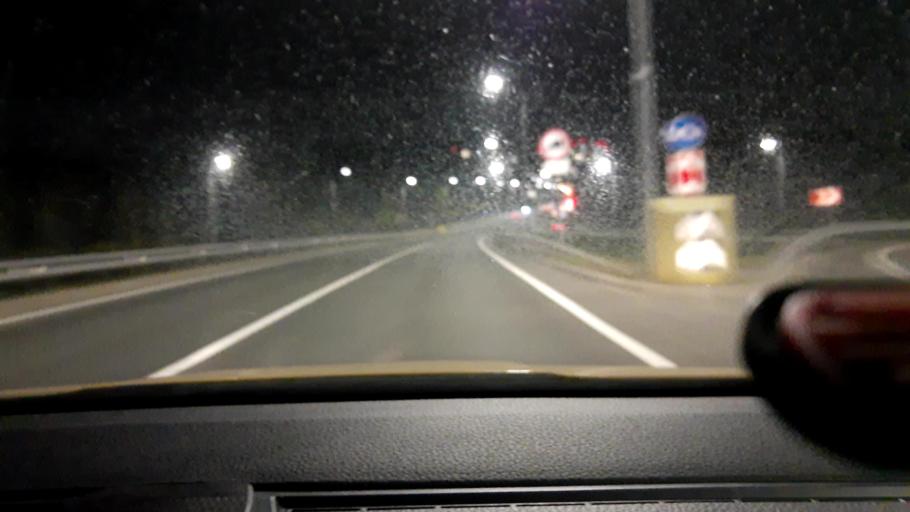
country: RU
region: Moskovskaya
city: Krasnoznamensk
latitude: 55.6081
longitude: 37.0532
